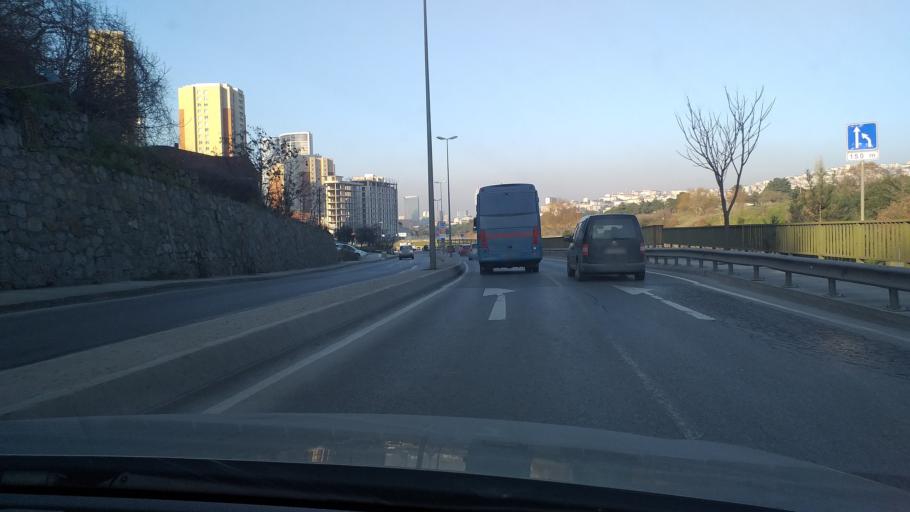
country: TR
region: Istanbul
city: Maltepe
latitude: 40.9216
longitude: 29.1897
